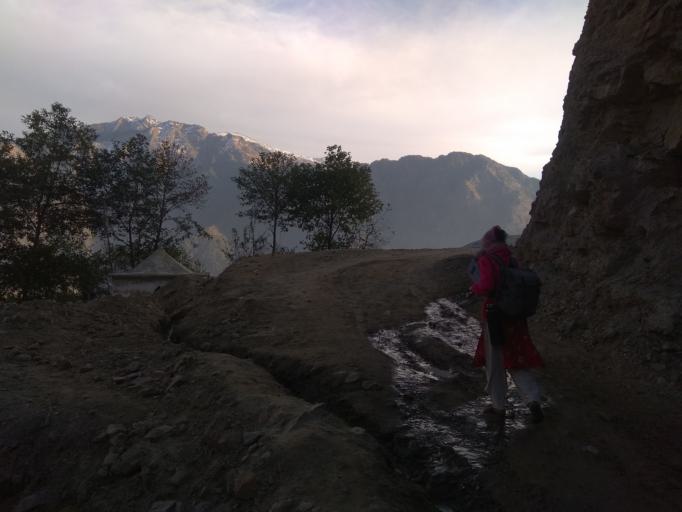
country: NP
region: Far Western
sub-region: Seti Zone
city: Achham
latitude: 29.2484
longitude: 81.6465
